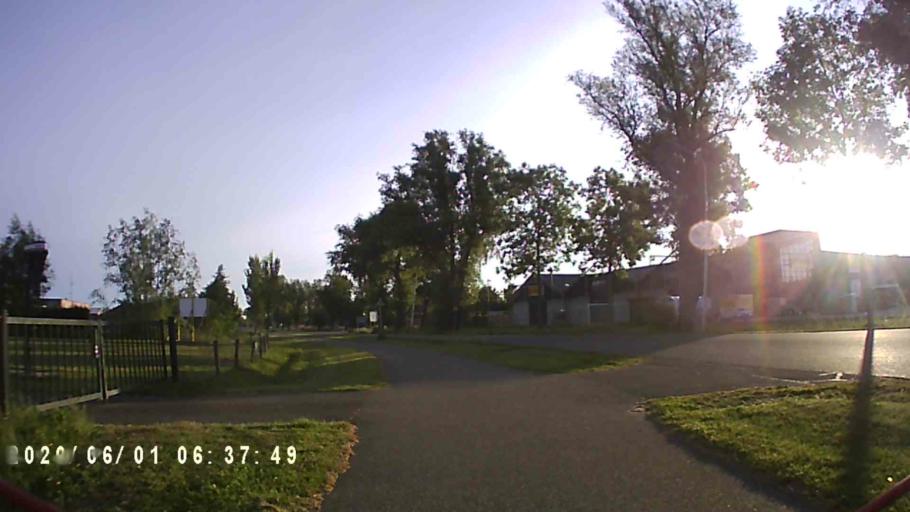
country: NL
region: Friesland
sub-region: Gemeente Kollumerland en Nieuwkruisland
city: Kollum
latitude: 53.2853
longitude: 6.1589
